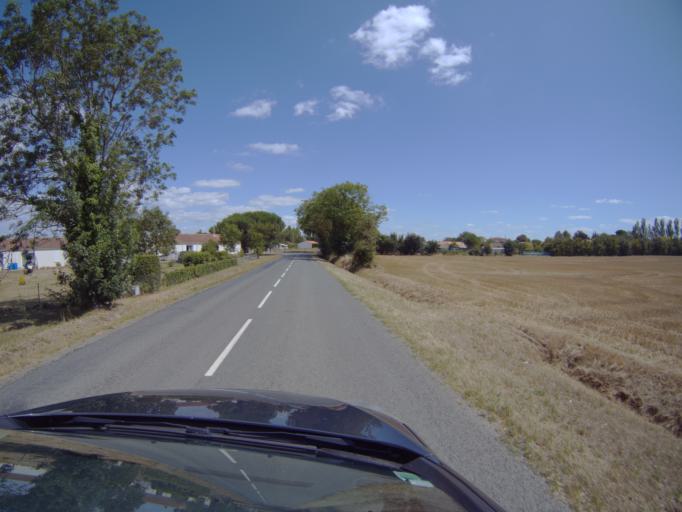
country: FR
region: Poitou-Charentes
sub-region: Departement de la Charente-Maritime
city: Courcon
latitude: 46.2472
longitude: -0.8186
